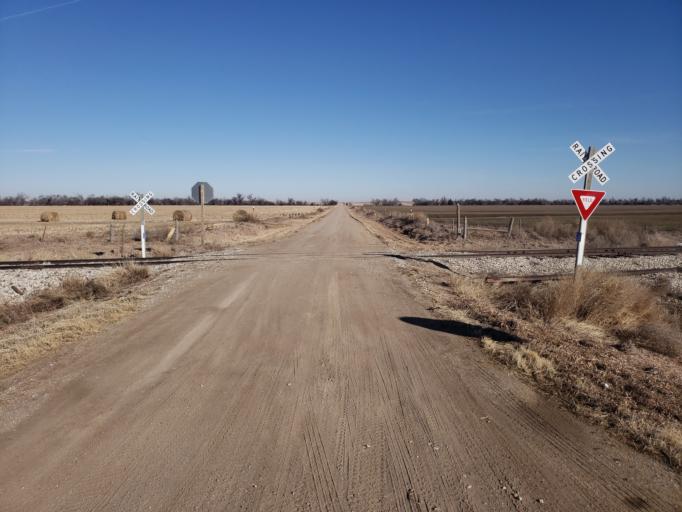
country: US
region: Kansas
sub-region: Ness County
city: Ness City
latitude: 38.4576
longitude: -99.6227
